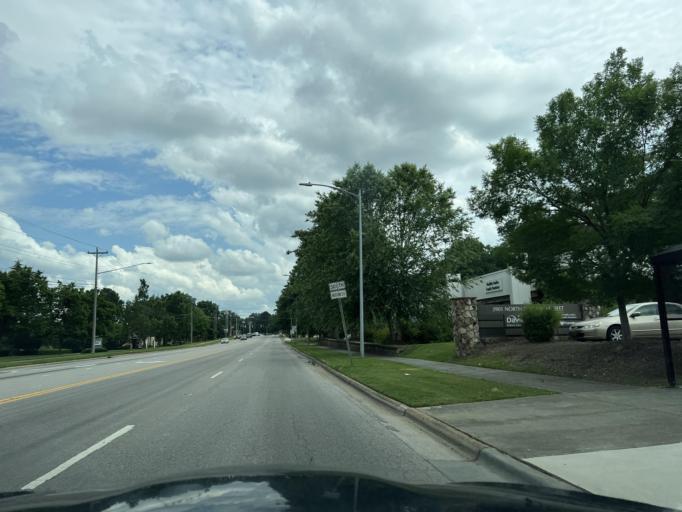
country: US
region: North Carolina
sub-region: Durham County
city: Durham
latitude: 36.0426
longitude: -78.9007
